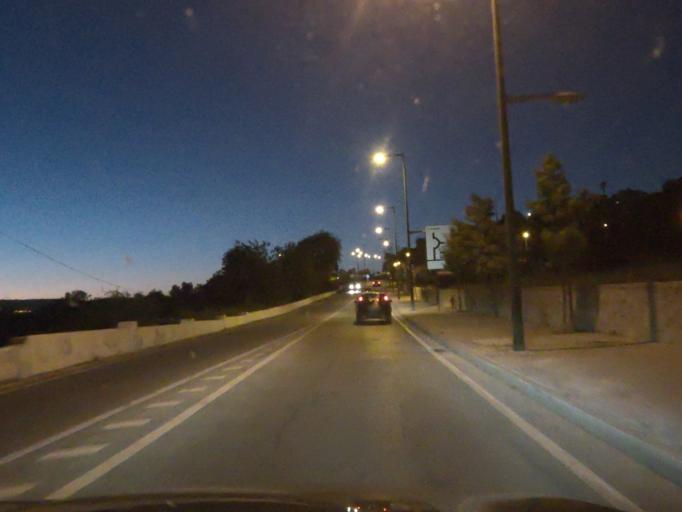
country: PT
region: Faro
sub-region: Loule
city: Loule
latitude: 37.1248
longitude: -8.0165
